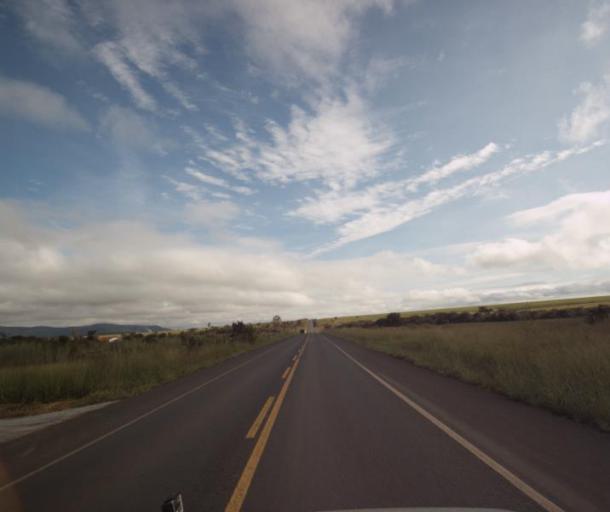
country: BR
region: Goias
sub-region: Padre Bernardo
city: Padre Bernardo
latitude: -15.4392
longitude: -48.6191
